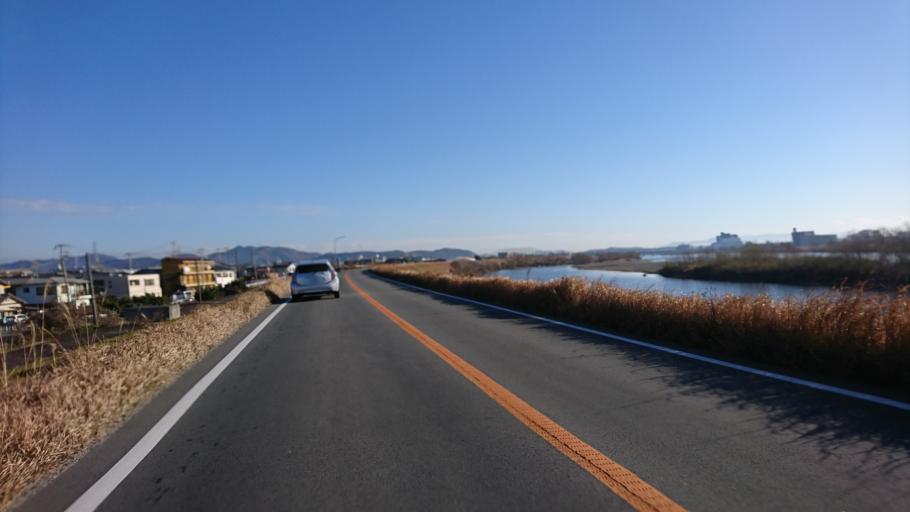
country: JP
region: Hyogo
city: Kakogawacho-honmachi
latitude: 34.7706
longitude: 134.8117
